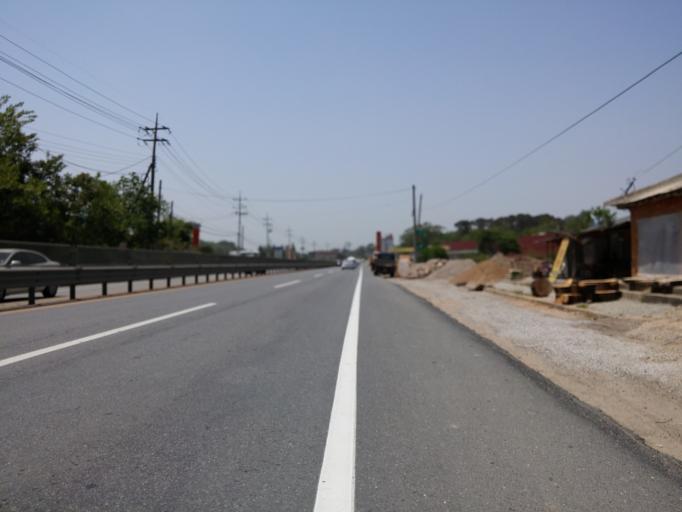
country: KR
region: Chungcheongnam-do
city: Nonsan
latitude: 36.2130
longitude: 127.1593
